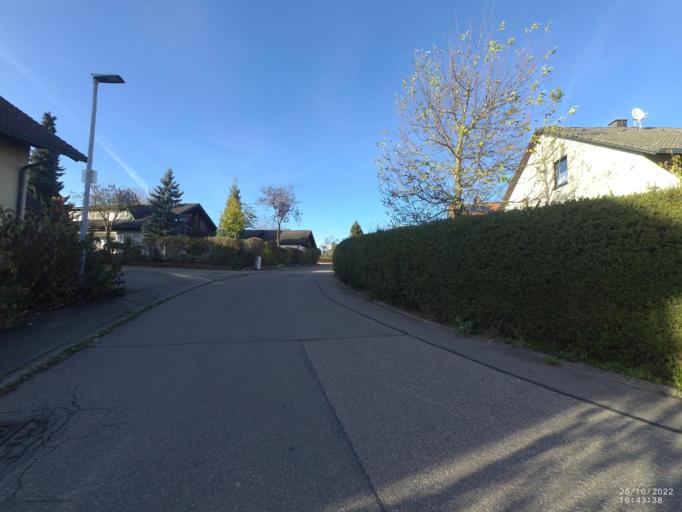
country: DE
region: Baden-Wuerttemberg
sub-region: Regierungsbezirk Stuttgart
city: Bohmenkirch
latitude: 48.6902
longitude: 9.9324
